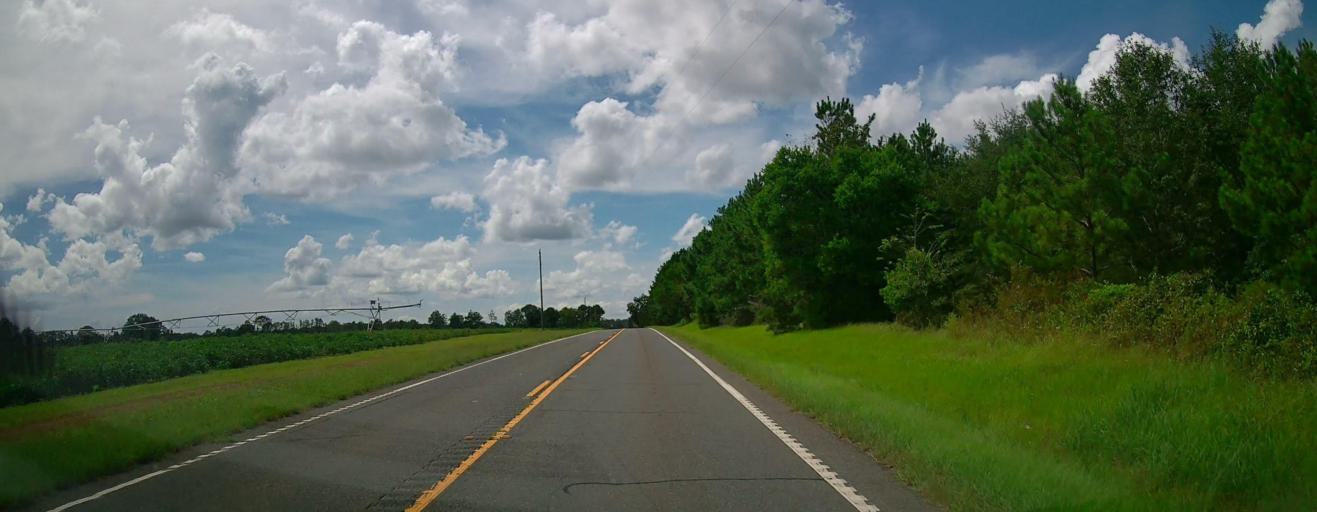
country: US
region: Georgia
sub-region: Macon County
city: Marshallville
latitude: 32.4336
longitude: -84.0614
